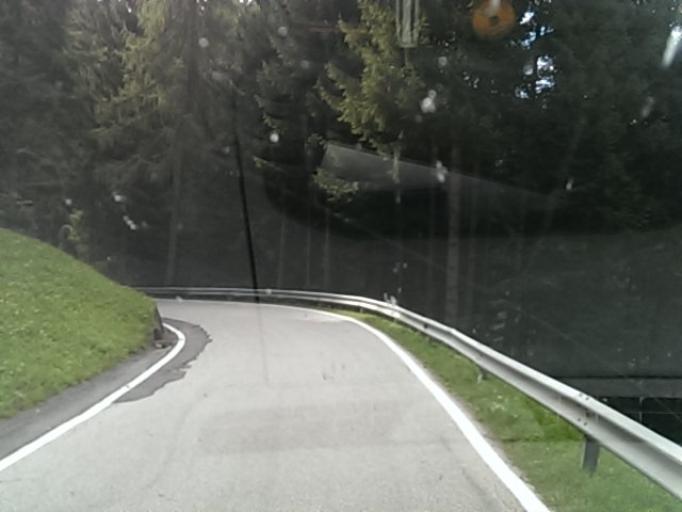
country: IT
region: Trentino-Alto Adige
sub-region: Bolzano
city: Lauregno
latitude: 46.4534
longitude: 11.0495
